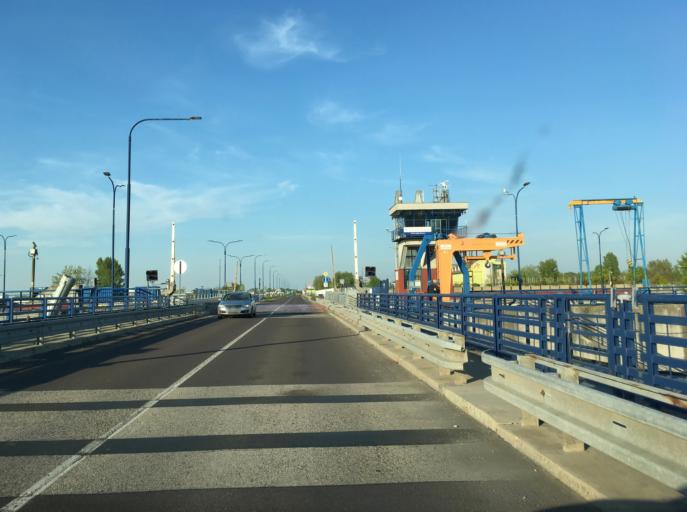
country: HU
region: Gyor-Moson-Sopron
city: Rajka
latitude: 48.0303
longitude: 17.2264
